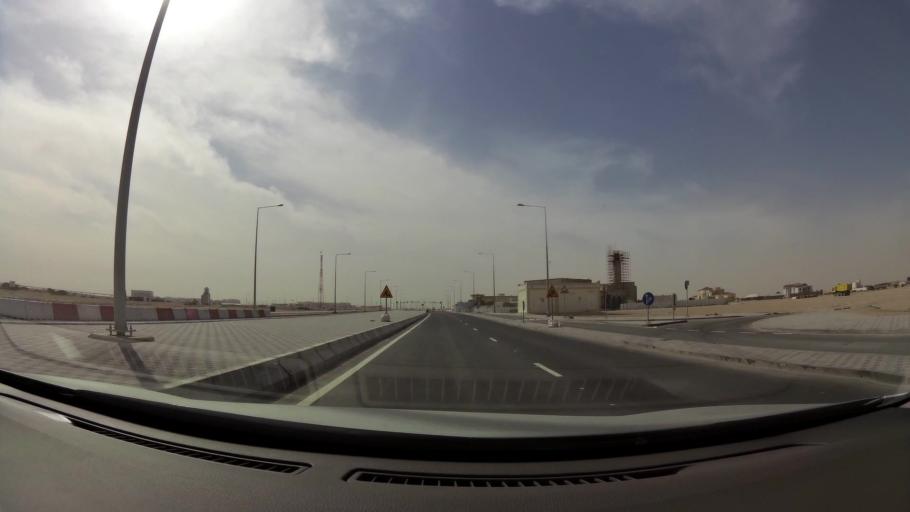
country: QA
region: Baladiyat ar Rayyan
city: Ar Rayyan
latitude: 25.3305
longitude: 51.3692
